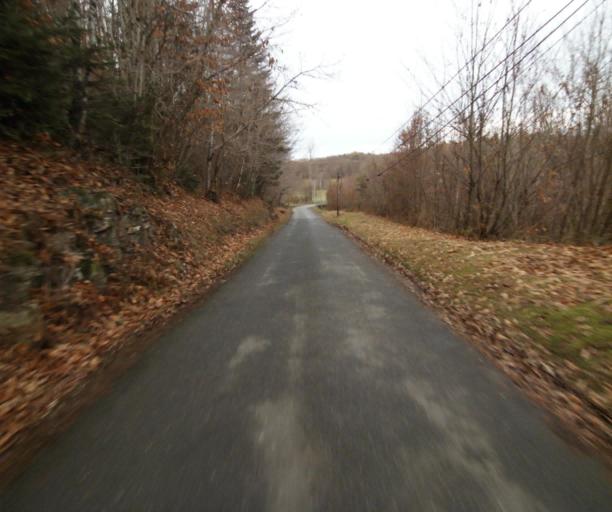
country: FR
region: Limousin
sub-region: Departement de la Correze
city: Chameyrat
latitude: 45.2357
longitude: 1.6880
